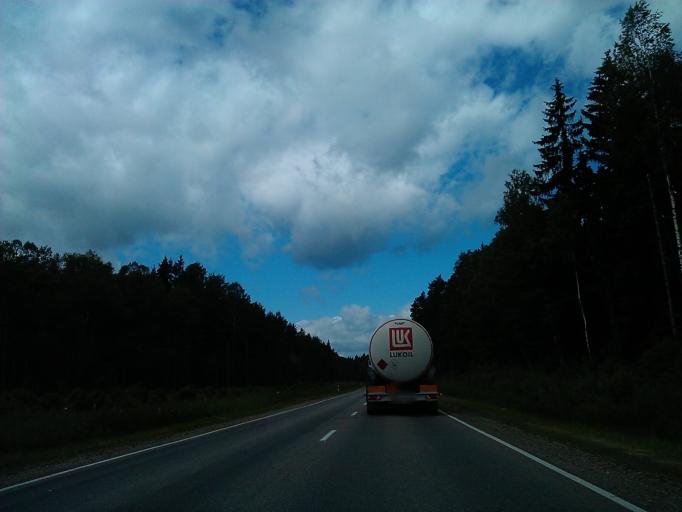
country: LV
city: Tireli
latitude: 56.9321
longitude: 23.4958
